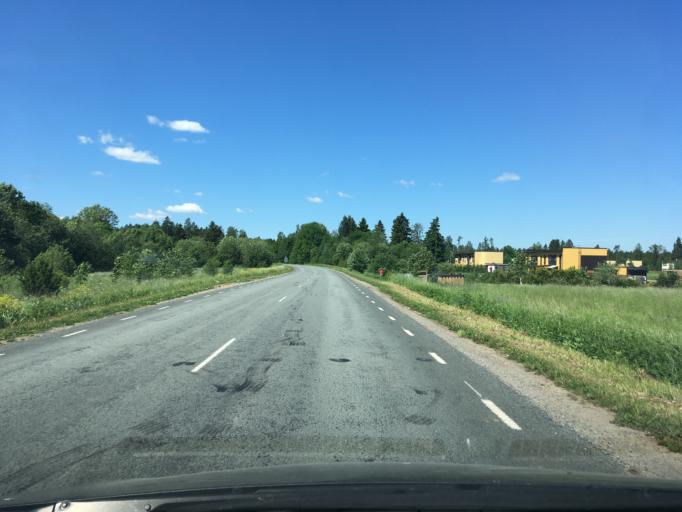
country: EE
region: Harju
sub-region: Rae vald
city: Vaida
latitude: 59.1952
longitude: 24.9883
